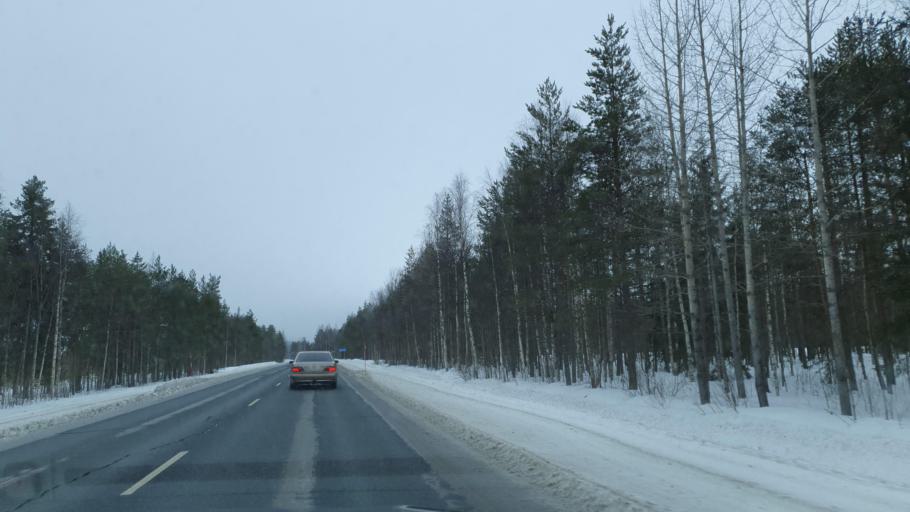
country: FI
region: Lapland
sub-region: Torniolaakso
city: Pello
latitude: 66.7303
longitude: 23.9135
